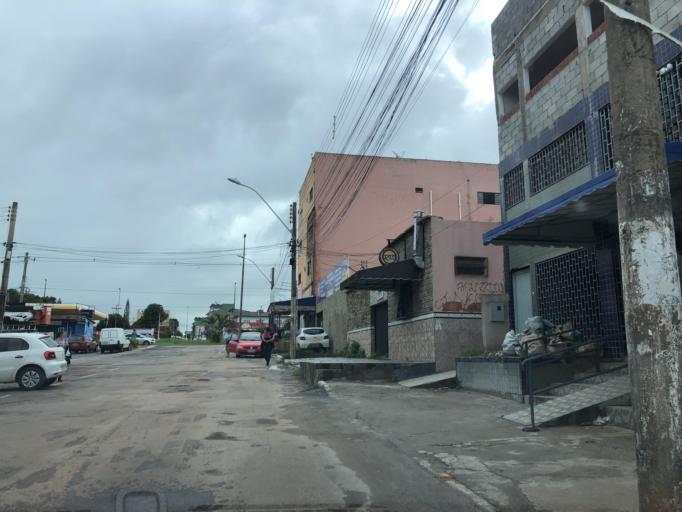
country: BR
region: Federal District
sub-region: Brasilia
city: Brasilia
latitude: -15.8340
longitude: -48.0940
